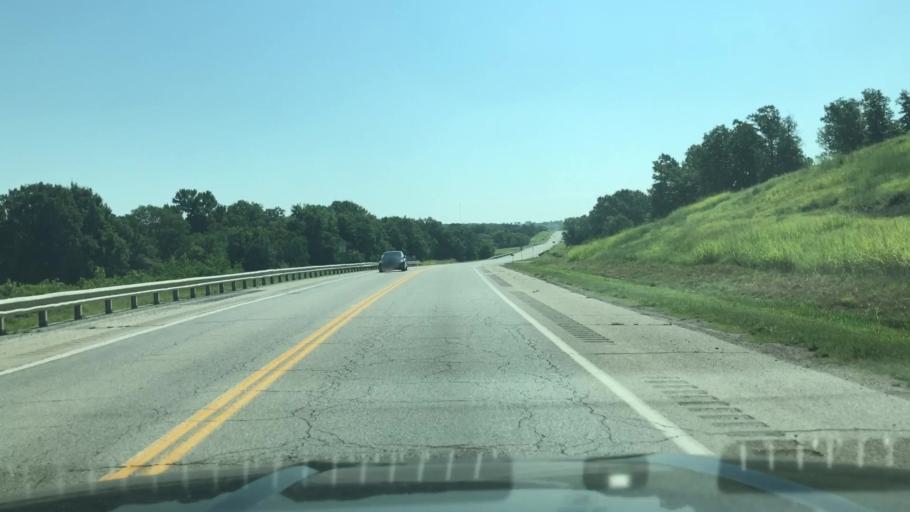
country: US
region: Oklahoma
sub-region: Creek County
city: Drumright
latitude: 35.9884
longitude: -96.5745
